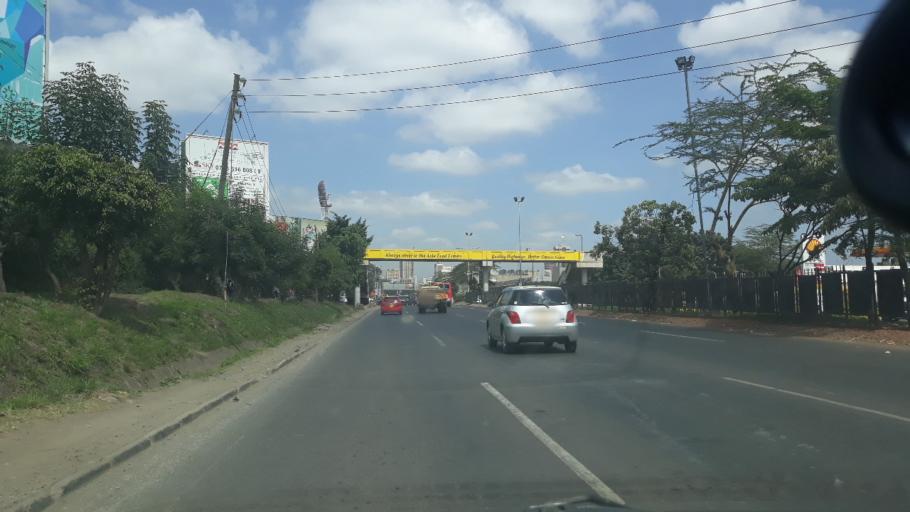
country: KE
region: Nairobi Area
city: Nairobi
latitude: -1.3064
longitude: 36.8271
